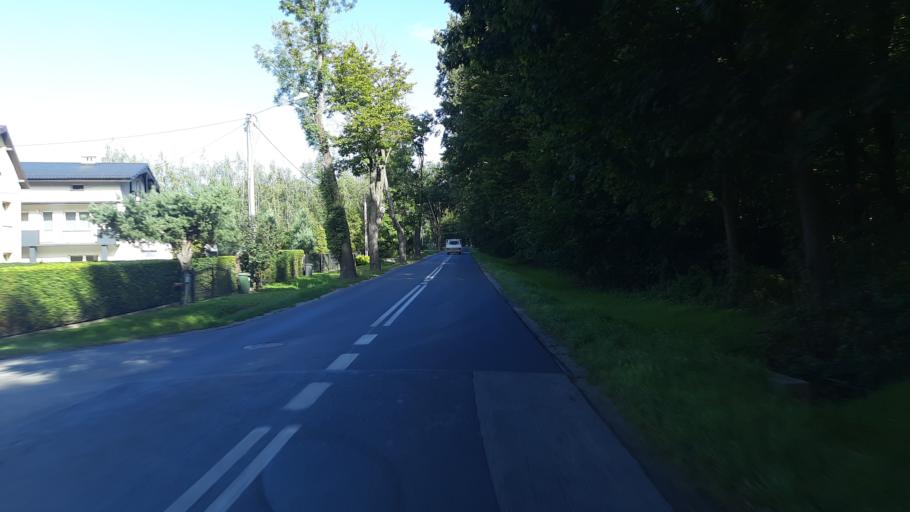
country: PL
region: Lower Silesian Voivodeship
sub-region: Powiat wroclawski
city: Dlugoleka
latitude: 51.1889
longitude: 17.1848
